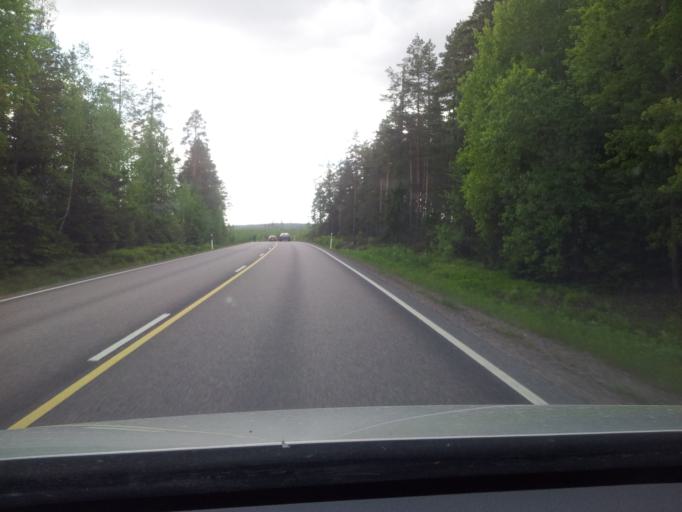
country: FI
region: Kymenlaakso
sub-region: Kouvola
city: Kouvola
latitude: 60.8539
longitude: 26.5494
